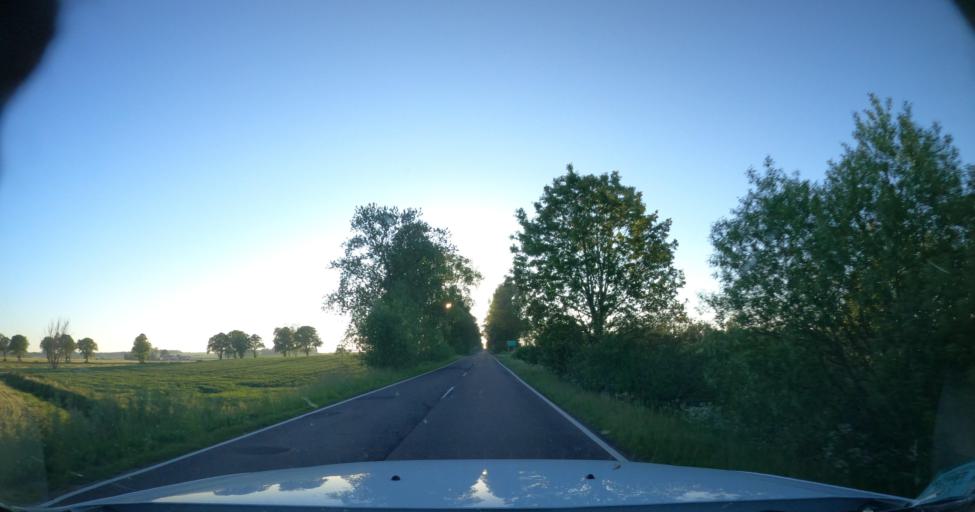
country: PL
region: Pomeranian Voivodeship
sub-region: Powiat slupski
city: Damnica
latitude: 54.4372
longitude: 17.3474
